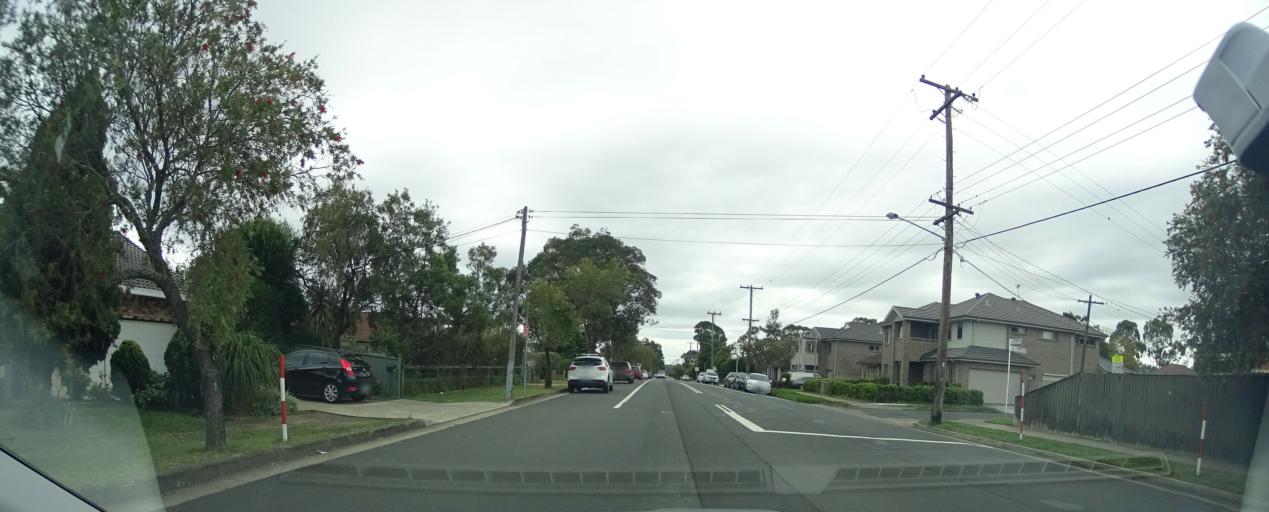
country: AU
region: New South Wales
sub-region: Bankstown
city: Revesby
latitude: -33.9702
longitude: 151.0078
